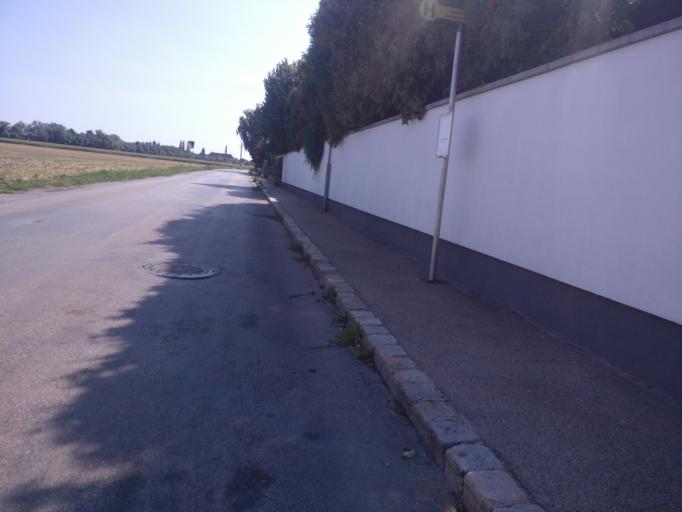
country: AT
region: Lower Austria
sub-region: Politischer Bezirk Modling
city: Guntramsdorf
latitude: 48.0382
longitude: 16.3105
